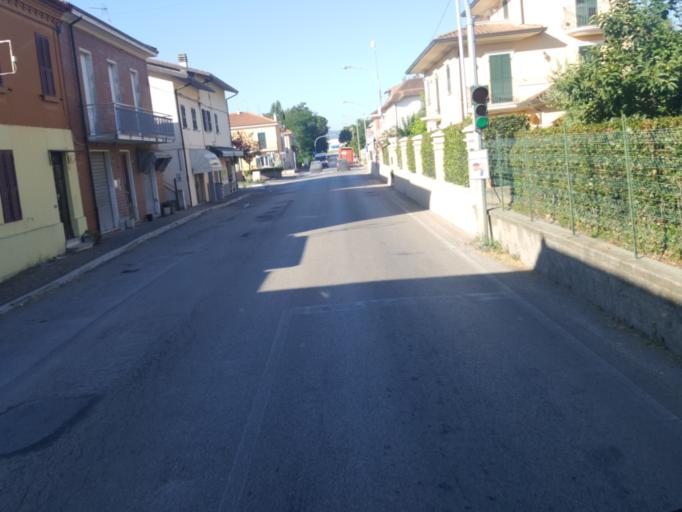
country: IT
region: The Marches
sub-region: Provincia di Pesaro e Urbino
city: Borgo Massano
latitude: 43.8307
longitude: 12.6835
